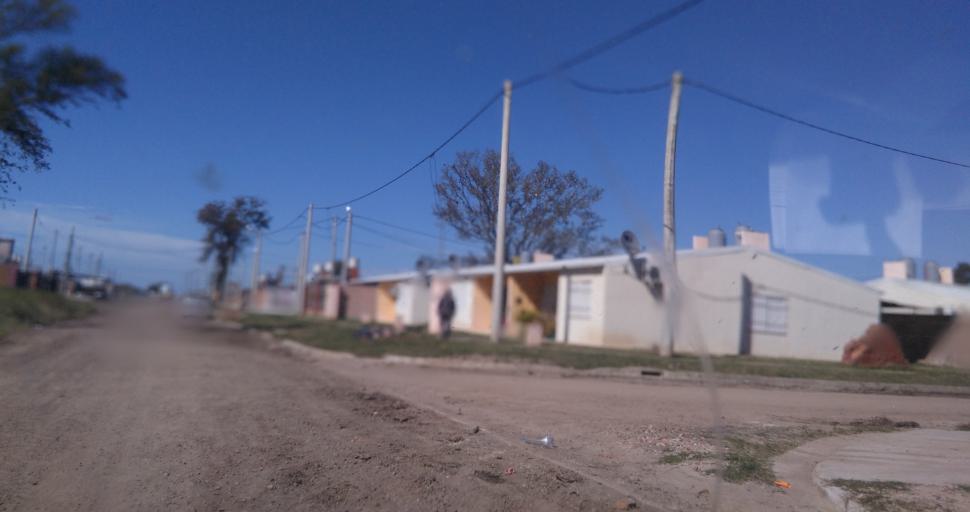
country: AR
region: Chaco
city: Fontana
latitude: -27.4563
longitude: -59.0507
